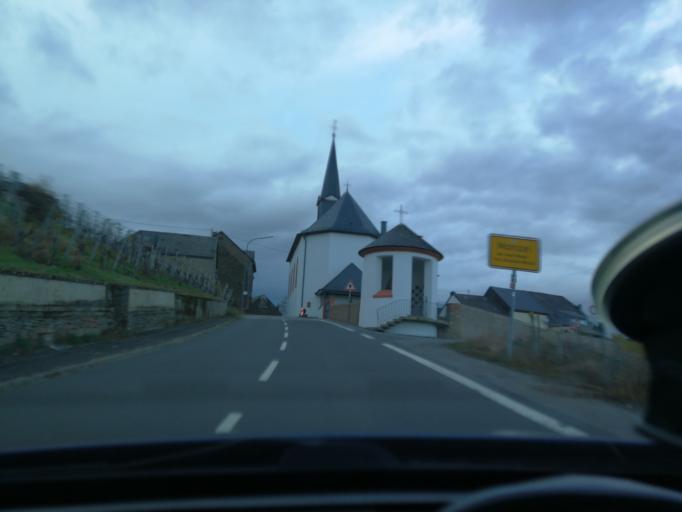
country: DE
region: Rheinland-Pfalz
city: Kesten
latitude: 49.9072
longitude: 6.9571
